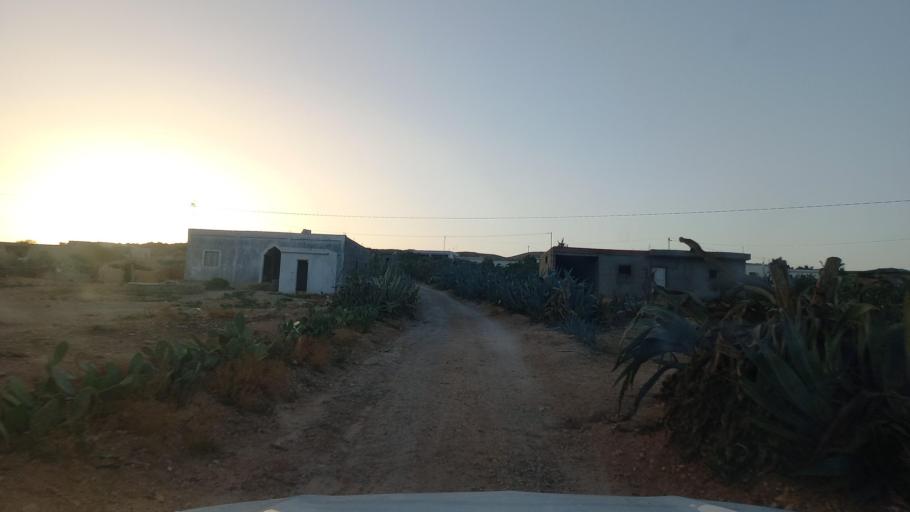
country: TN
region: Al Qasrayn
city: Sbiba
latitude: 35.3757
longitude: 9.0105
